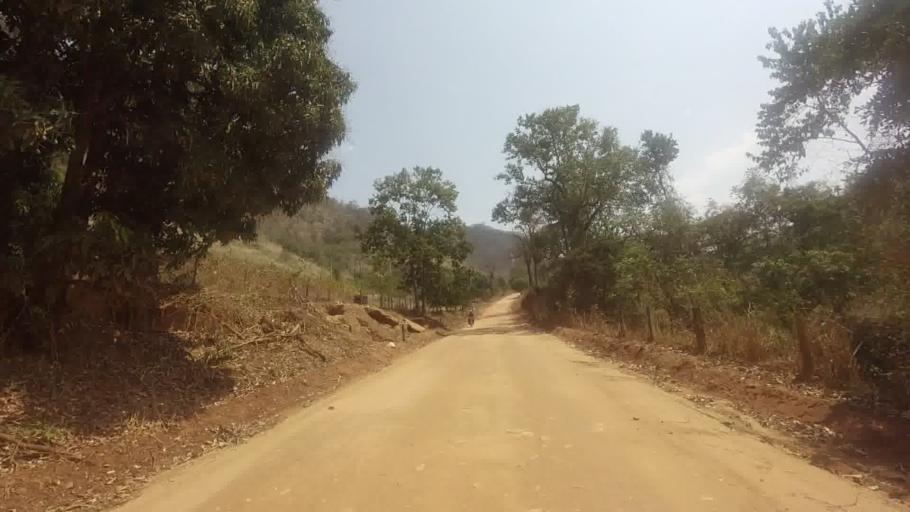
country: BR
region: Espirito Santo
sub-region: Mimoso Do Sul
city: Mimoso do Sul
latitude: -20.9474
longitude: -41.3827
